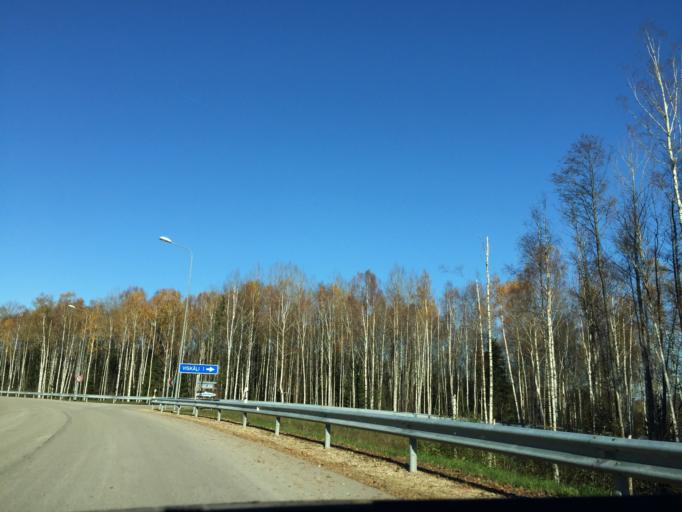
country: LV
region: Aizkraukles Rajons
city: Aizkraukle
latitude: 56.7034
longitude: 25.2829
